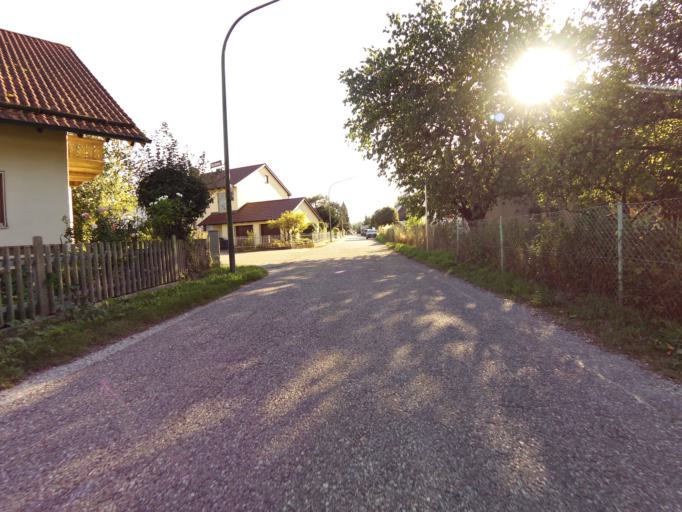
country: DE
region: Bavaria
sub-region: Lower Bavaria
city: Stallwang
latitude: 48.5692
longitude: 12.2031
